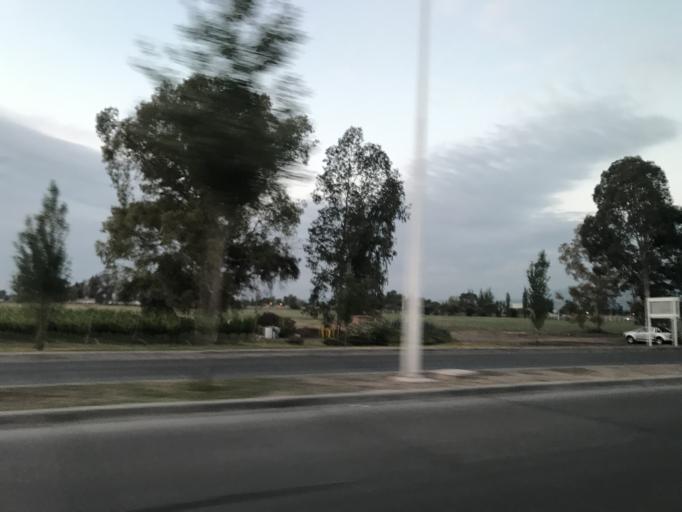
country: AR
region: Mendoza
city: Las Heras
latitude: -32.8277
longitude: -68.8023
